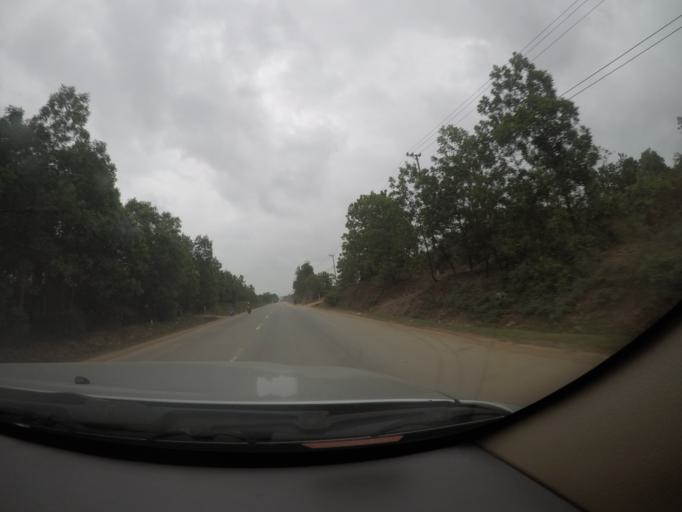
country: VN
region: Quang Tri
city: Dong Ha
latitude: 16.7901
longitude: 107.0815
